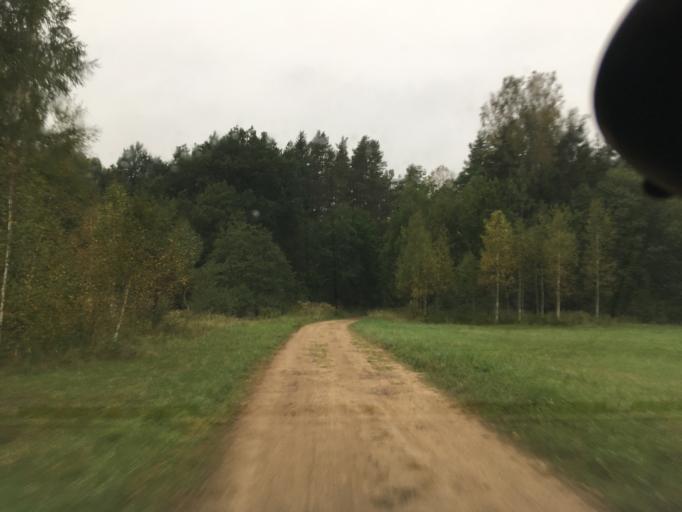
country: LV
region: Kuldigas Rajons
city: Kuldiga
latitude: 56.9866
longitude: 22.0133
